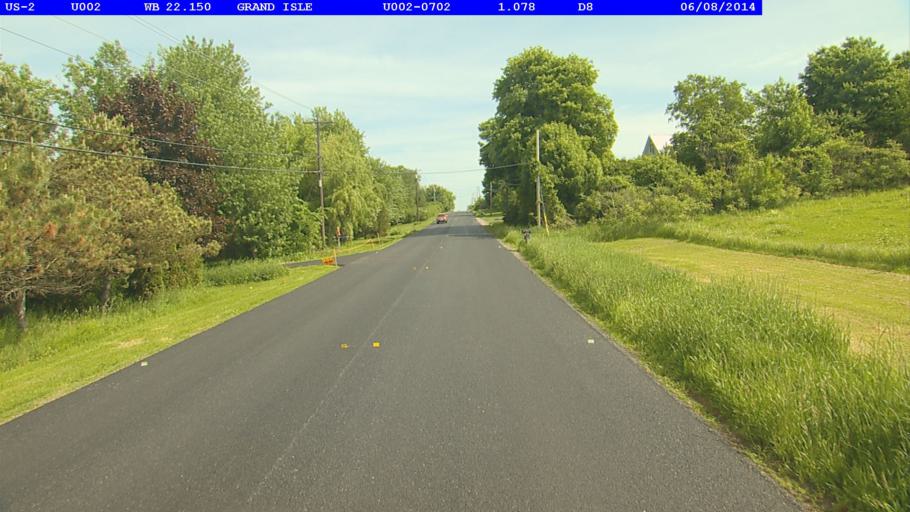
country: US
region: Vermont
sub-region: Grand Isle County
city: North Hero
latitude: 44.7518
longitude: -73.2873
